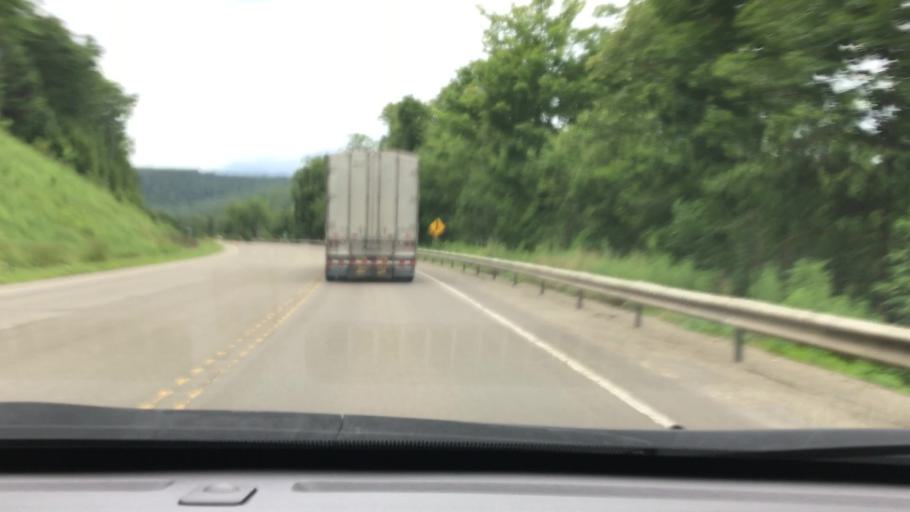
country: US
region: Pennsylvania
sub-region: McKean County
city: Kane
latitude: 41.7598
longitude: -78.7000
